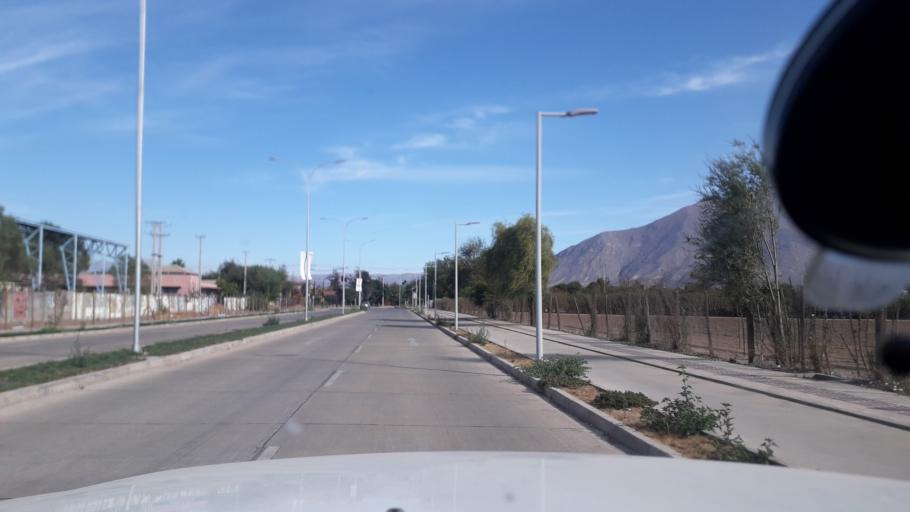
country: CL
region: Valparaiso
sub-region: Provincia de San Felipe
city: San Felipe
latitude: -32.7484
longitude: -70.7108
